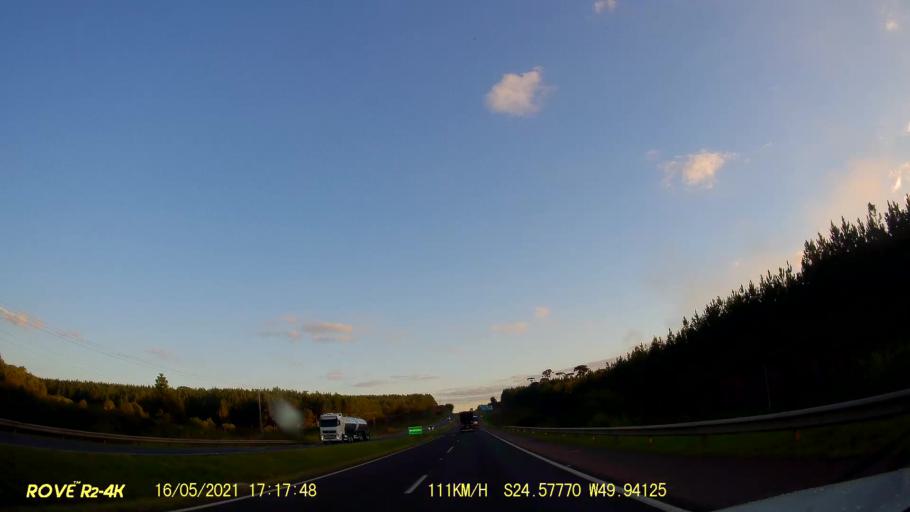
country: BR
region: Parana
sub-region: Pirai Do Sul
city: Pirai do Sul
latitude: -24.5779
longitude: -49.9414
